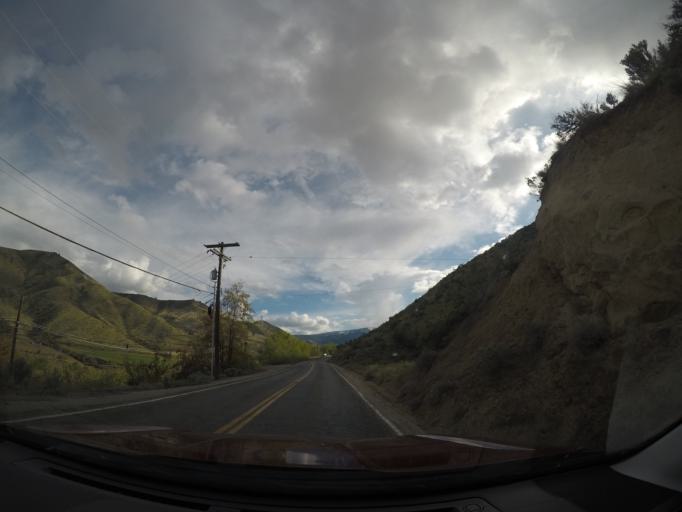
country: US
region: Washington
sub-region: Chelan County
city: South Wenatchee
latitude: 47.3849
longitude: -120.3117
